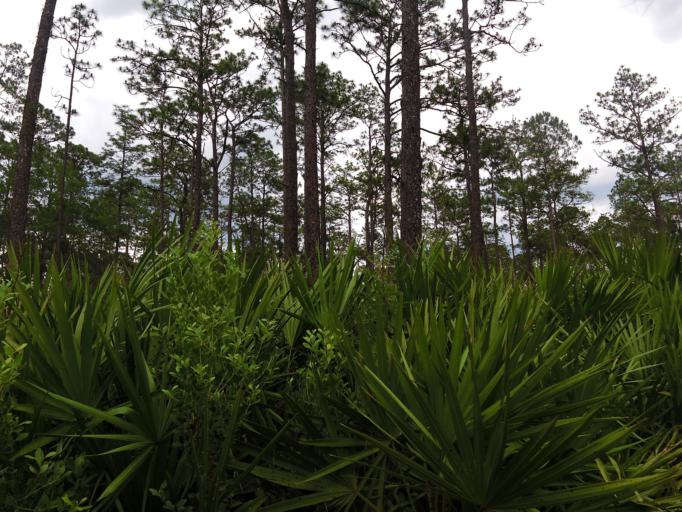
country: US
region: Florida
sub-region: Union County
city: Lake Butler
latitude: 30.2158
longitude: -82.3888
